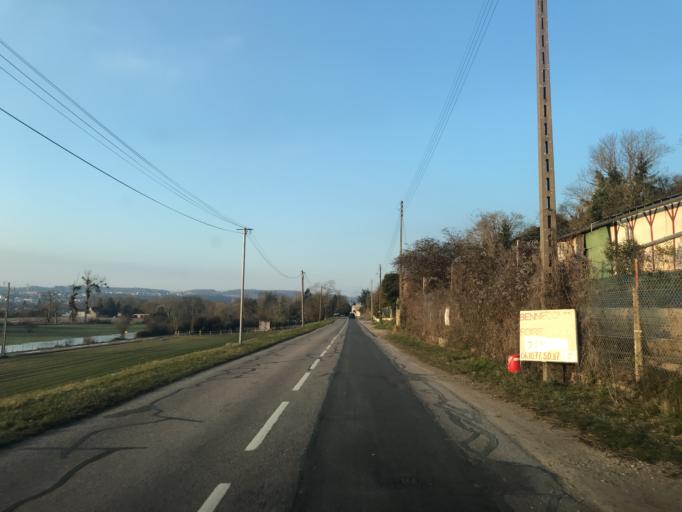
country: FR
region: Ile-de-France
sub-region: Departement des Yvelines
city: Freneuse
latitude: 49.0491
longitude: 1.5861
